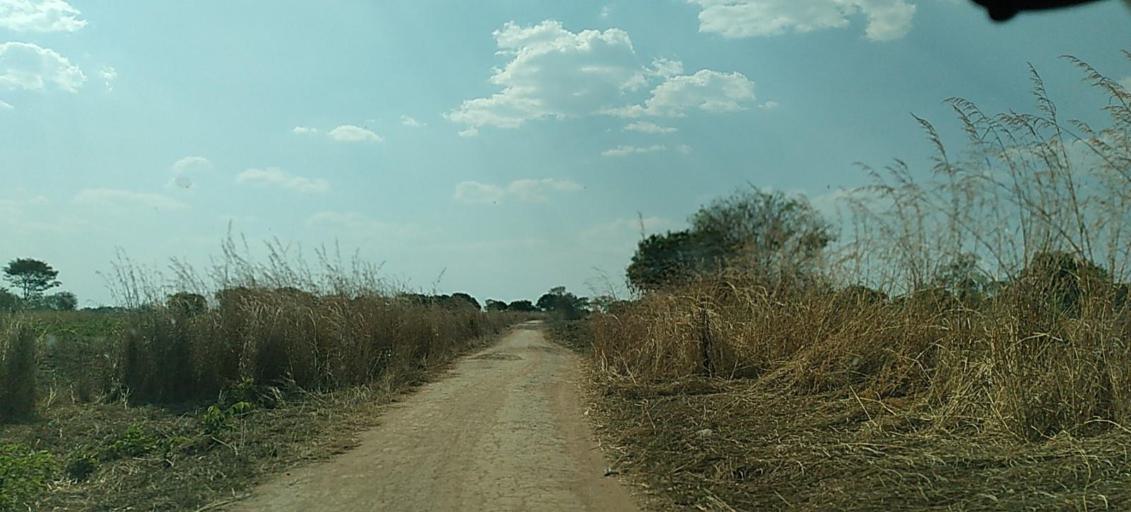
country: ZM
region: North-Western
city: Kalengwa
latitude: -13.0969
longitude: 24.9793
